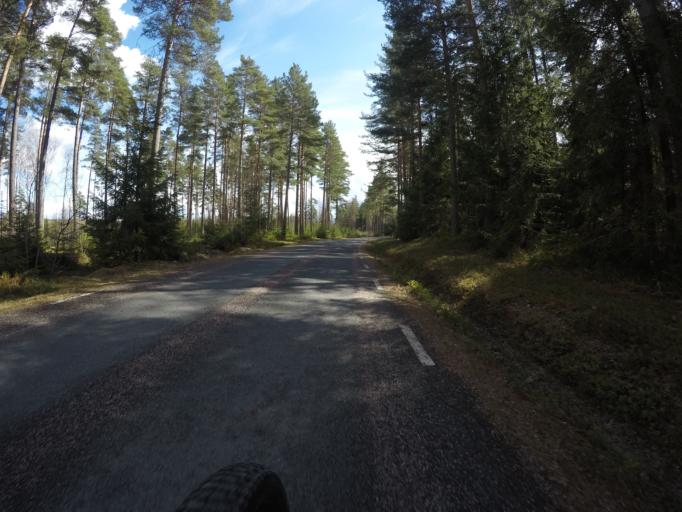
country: SE
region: Vaestmanland
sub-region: Kungsors Kommun
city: Kungsoer
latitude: 59.3172
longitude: 16.1161
